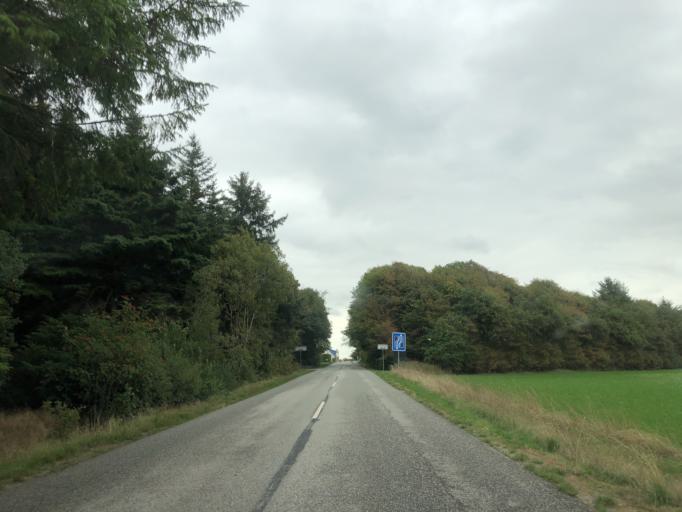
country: DK
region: Central Jutland
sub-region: Herning Kommune
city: Vildbjerg
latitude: 56.1817
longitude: 8.8311
